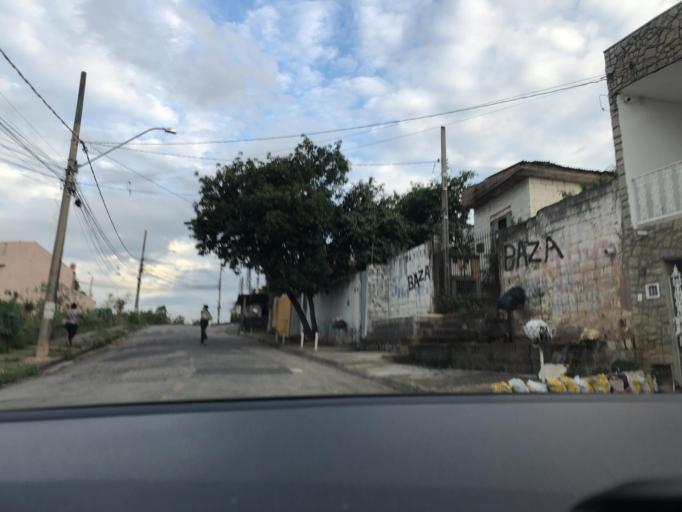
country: BR
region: Sao Paulo
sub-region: Varzea Paulista
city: Varzea Paulista
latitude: -23.2179
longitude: -46.8518
